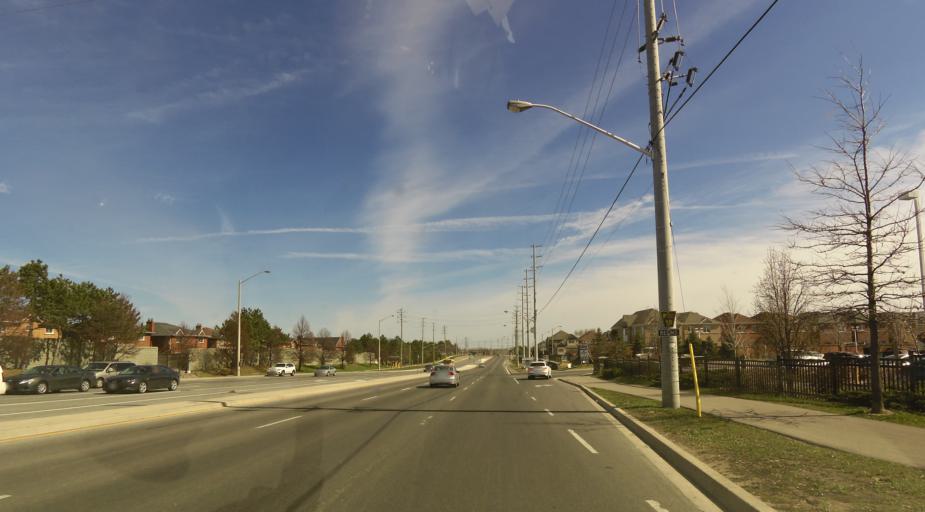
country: CA
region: Ontario
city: Brampton
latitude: 43.6461
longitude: -79.7538
